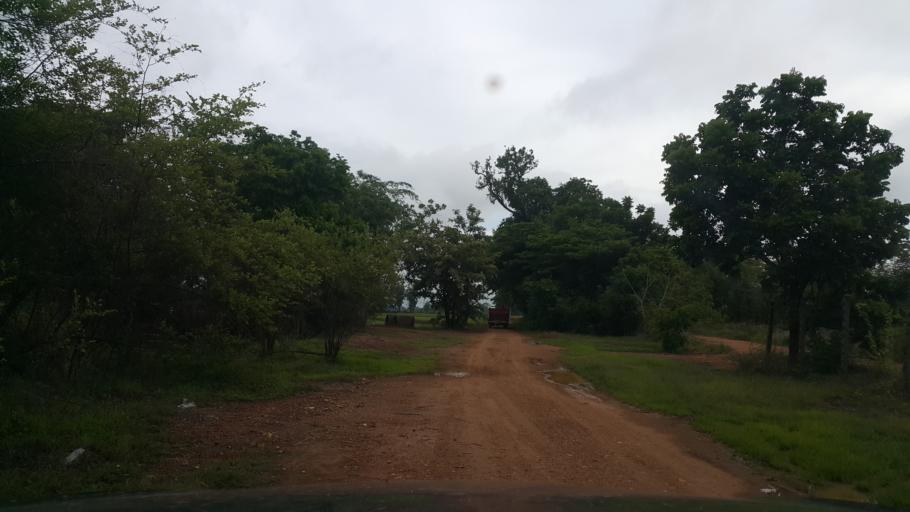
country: TH
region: Sukhothai
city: Sawankhalok
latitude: 17.3063
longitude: 99.7134
